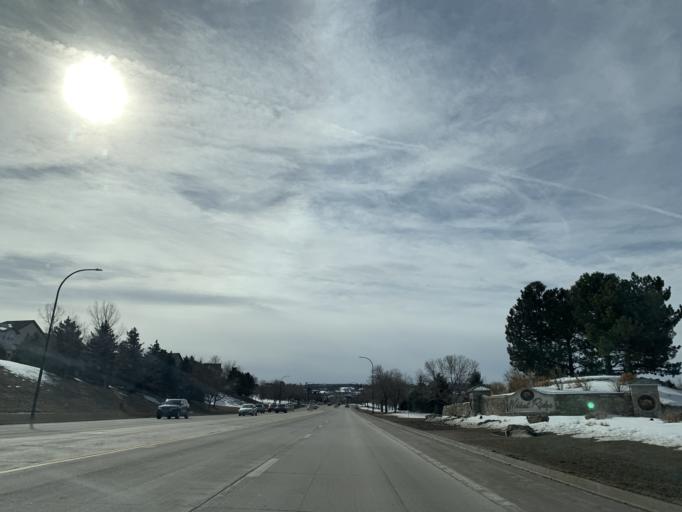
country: US
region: Colorado
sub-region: Douglas County
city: Carriage Club
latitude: 39.5286
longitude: -104.9172
